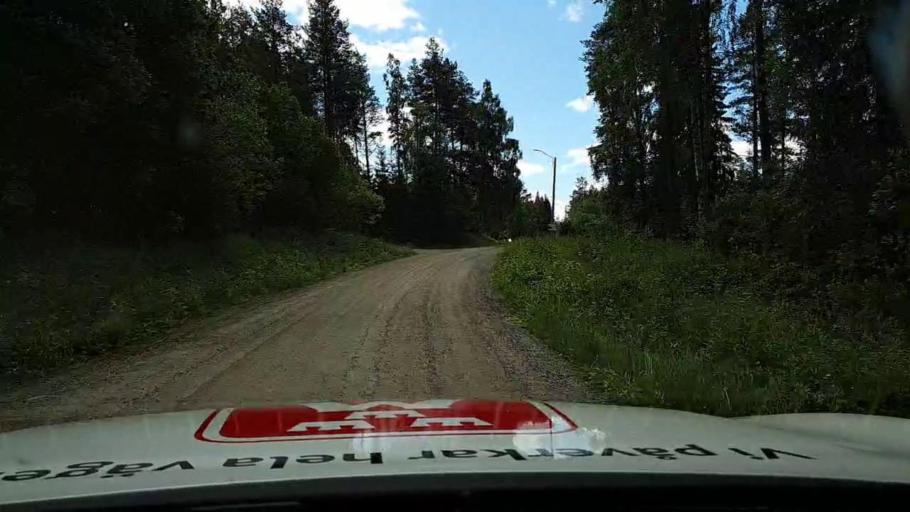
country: SE
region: Jaemtland
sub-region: Braecke Kommun
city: Braecke
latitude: 62.7560
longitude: 15.5033
